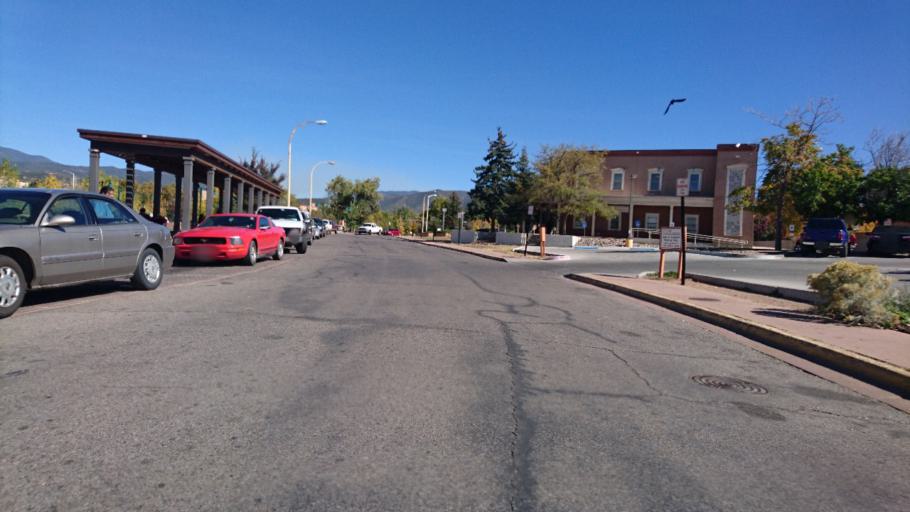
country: US
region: New Mexico
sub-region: Santa Fe County
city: Santa Fe
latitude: 35.6863
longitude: -105.9446
